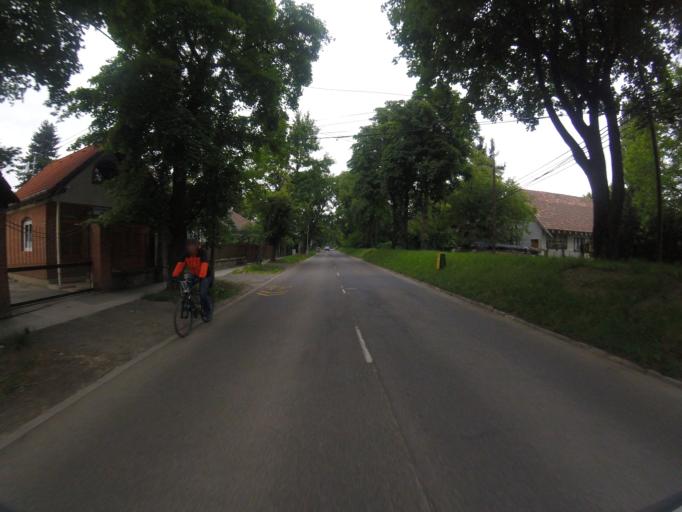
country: HU
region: Budapest
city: Budapest IV. keruelet
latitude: 47.5803
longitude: 19.0641
